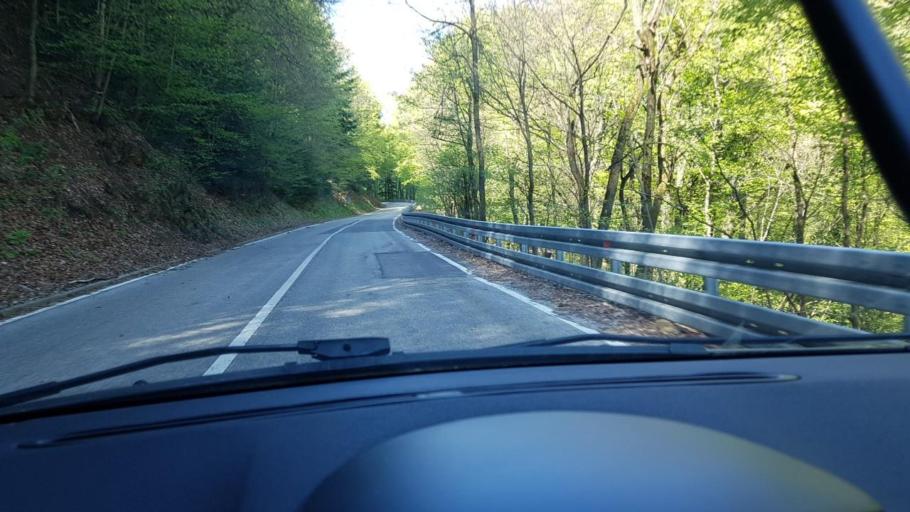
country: HR
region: Grad Zagreb
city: Kasina
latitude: 45.9415
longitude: 15.9741
